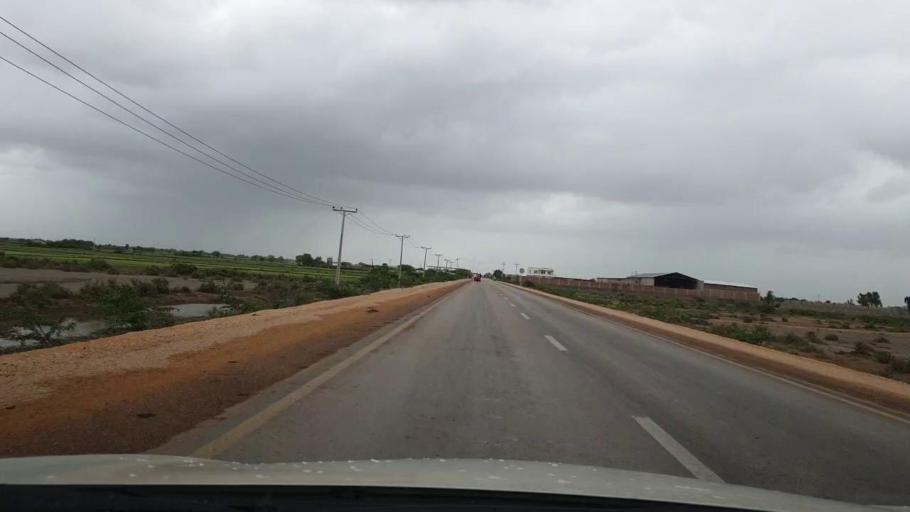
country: PK
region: Sindh
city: Badin
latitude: 24.6530
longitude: 68.7696
